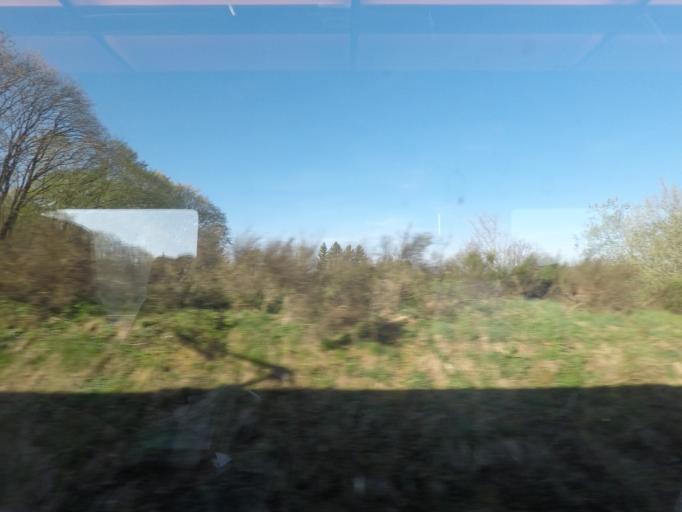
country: BE
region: Wallonia
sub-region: Province du Luxembourg
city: Neufchateau
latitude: 49.8127
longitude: 5.4823
